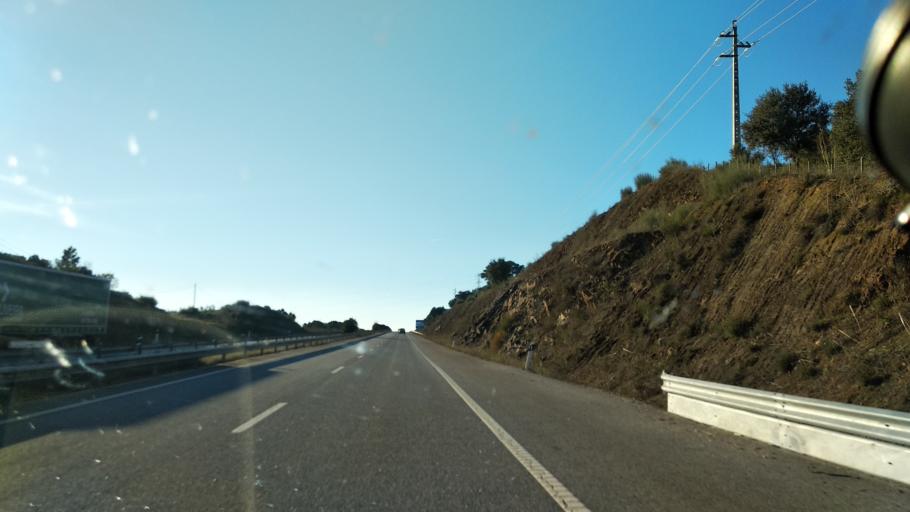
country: PT
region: Santarem
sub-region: Abrantes
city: Alferrarede
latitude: 39.4859
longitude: -8.1318
